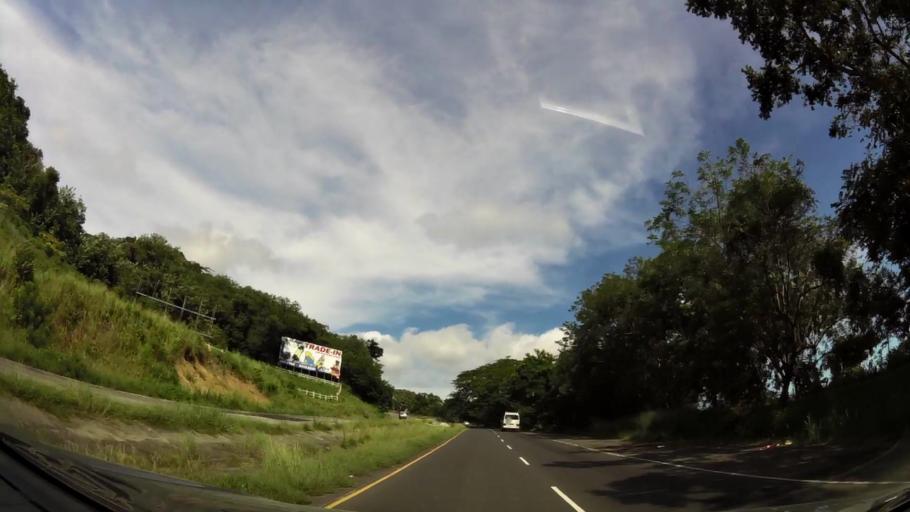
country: PA
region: Panama
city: Capira
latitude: 8.7041
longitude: -79.8712
